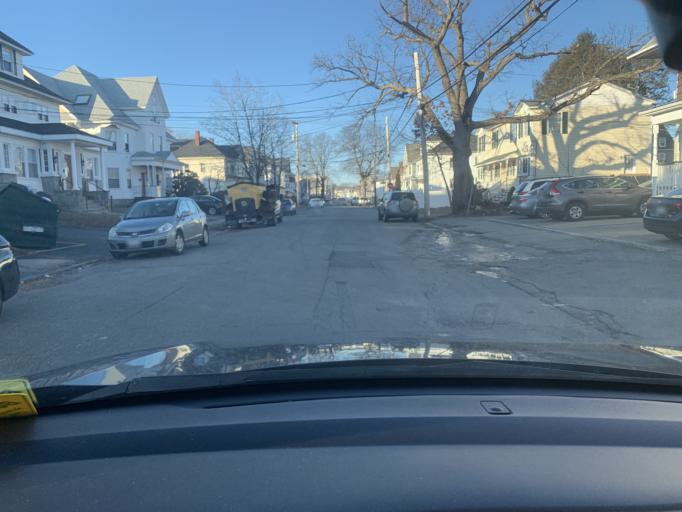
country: US
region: Massachusetts
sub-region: Essex County
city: North Andover
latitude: 42.6986
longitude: -71.1504
